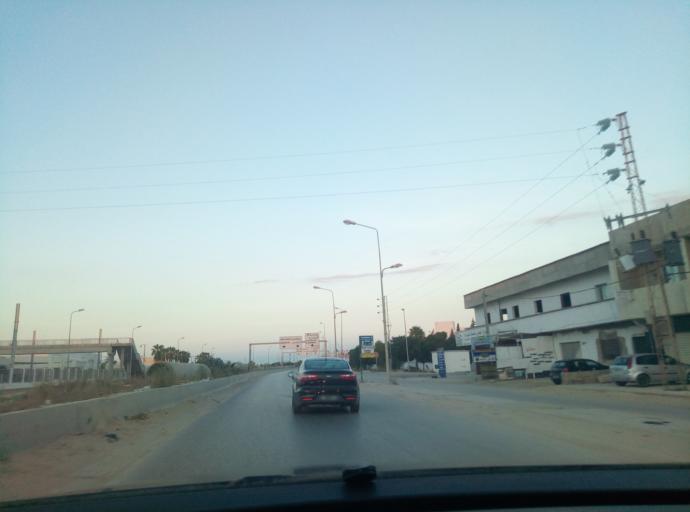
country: TN
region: Manouba
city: Manouba
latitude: 36.7831
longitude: 10.1142
